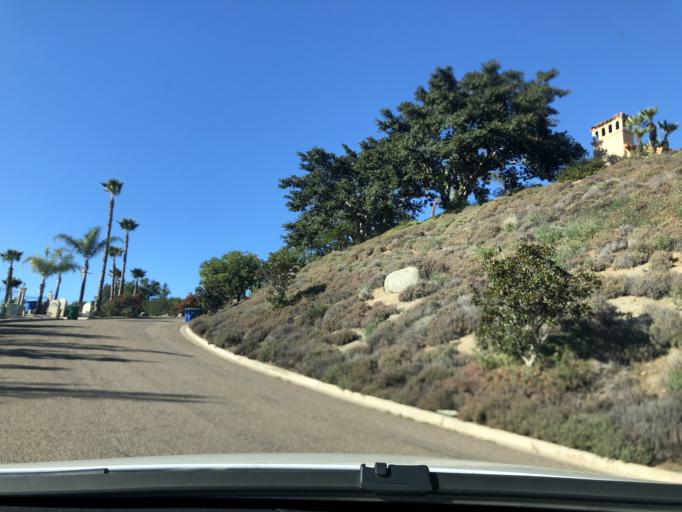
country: US
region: California
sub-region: San Diego County
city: Bostonia
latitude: 32.7810
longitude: -116.9382
